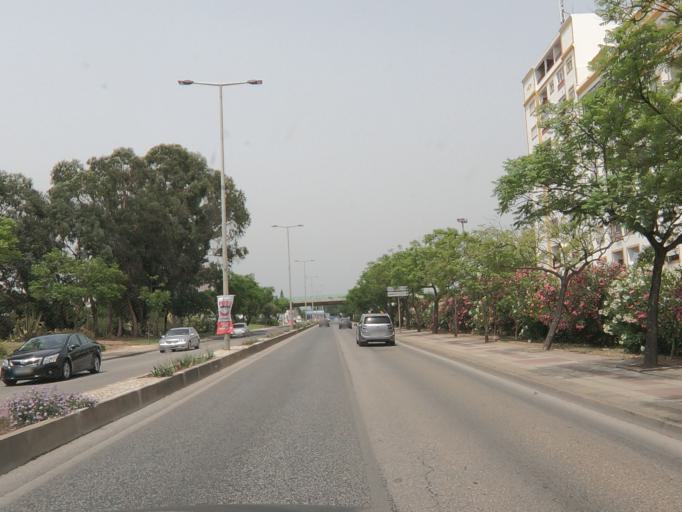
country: PT
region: Faro
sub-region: Portimao
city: Portimao
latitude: 37.1353
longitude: -8.5455
